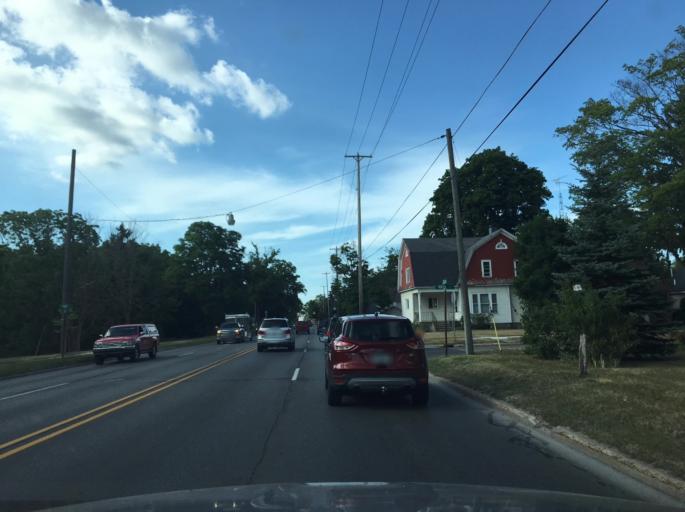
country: US
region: Michigan
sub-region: Grand Traverse County
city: Traverse City
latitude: 44.7579
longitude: -85.6347
